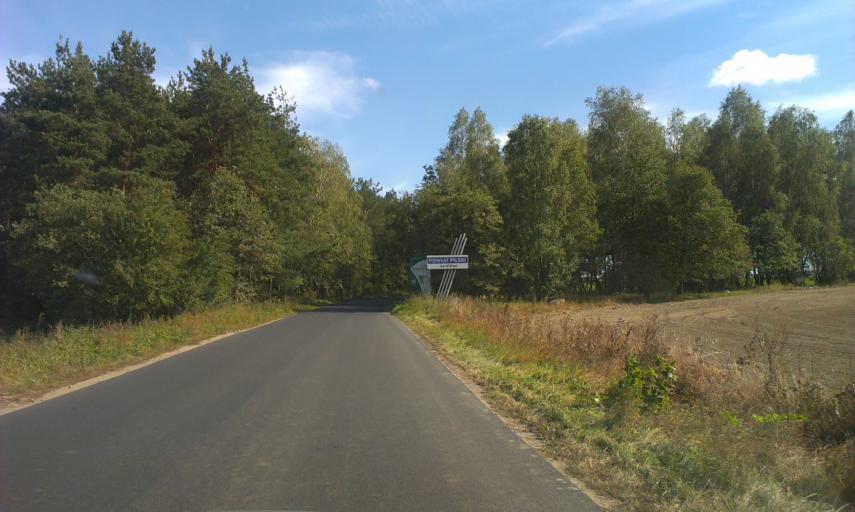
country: PL
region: Greater Poland Voivodeship
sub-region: Powiat pilski
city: Lobzenica
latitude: 53.2836
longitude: 17.1844
